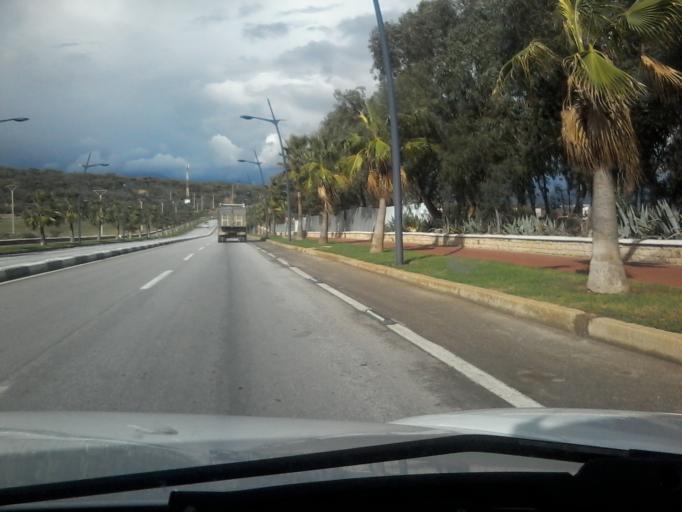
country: ES
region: Ceuta
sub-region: Ceuta
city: Ceuta
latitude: 35.7673
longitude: -5.3489
